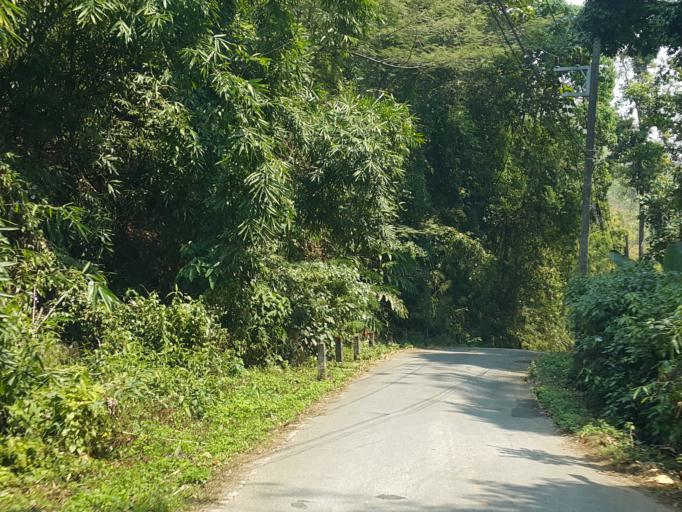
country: TH
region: Lampang
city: Mueang Pan
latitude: 18.8185
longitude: 99.4353
